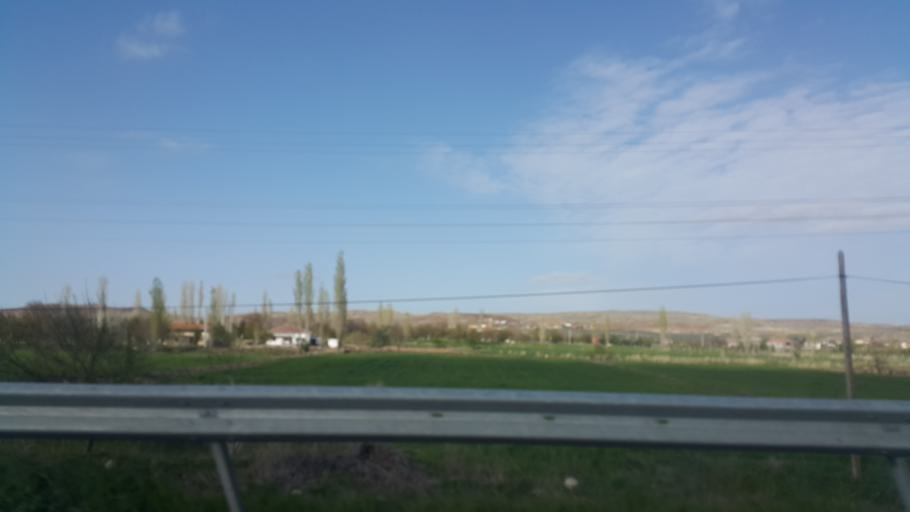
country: TR
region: Aksaray
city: Acipinar
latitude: 38.4945
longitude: 33.8747
